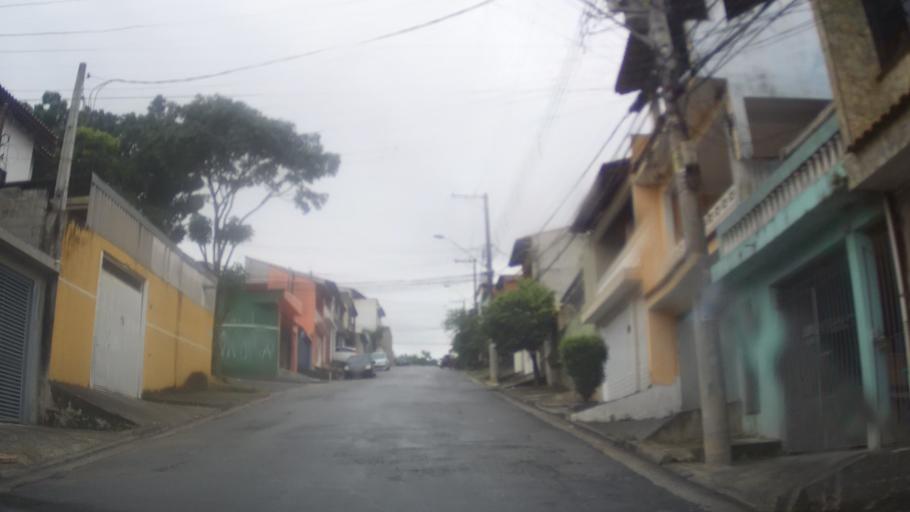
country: BR
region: Sao Paulo
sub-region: Guarulhos
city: Guarulhos
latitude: -23.4384
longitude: -46.5331
